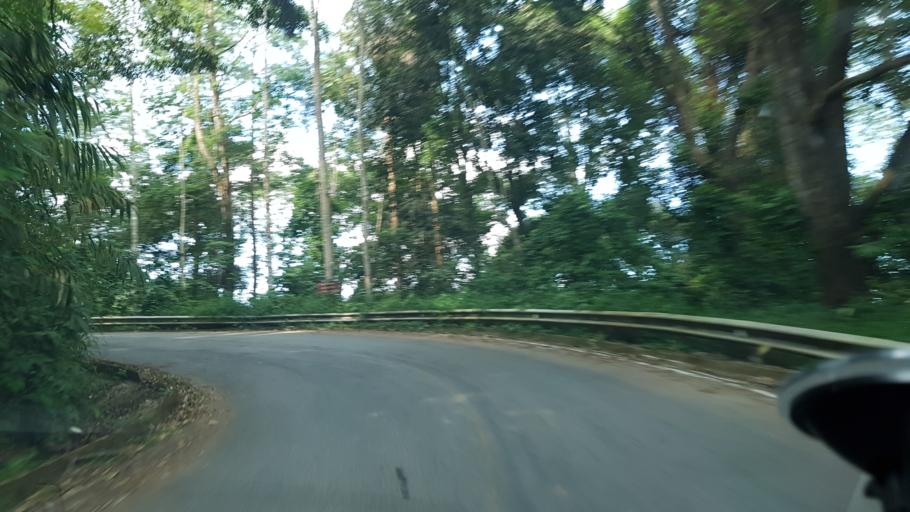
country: TH
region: Chiang Rai
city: Mae Fa Luang
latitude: 20.3274
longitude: 99.8198
